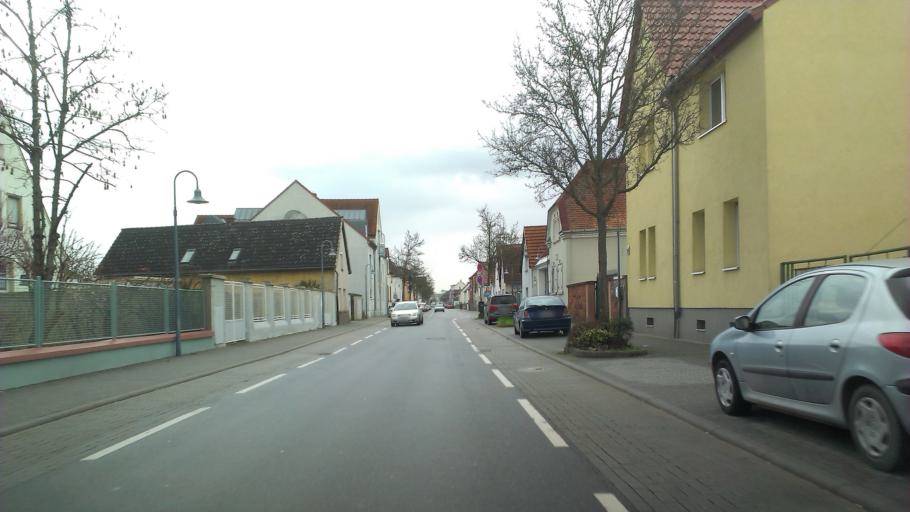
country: DE
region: Rheinland-Pfalz
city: Frankenthal
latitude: 49.4966
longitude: 8.3689
